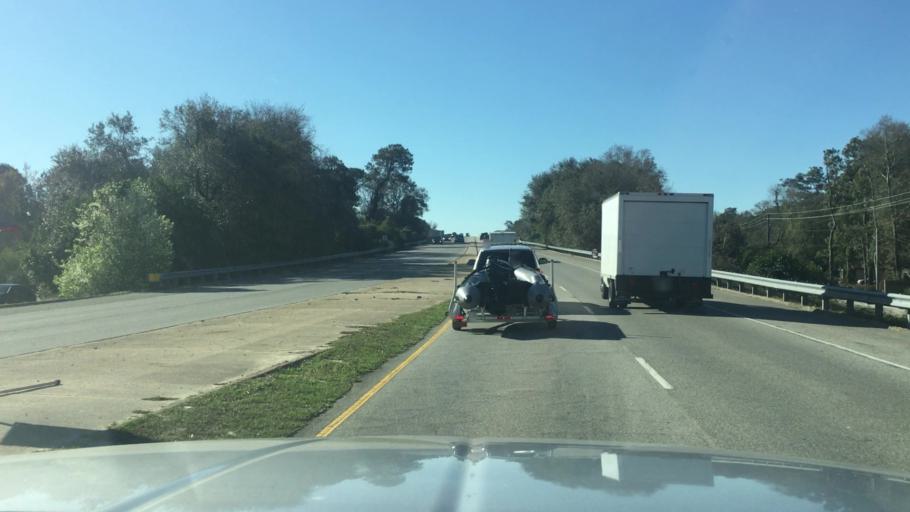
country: US
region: North Carolina
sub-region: New Hanover County
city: Sea Breeze
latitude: 34.0606
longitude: -77.8995
